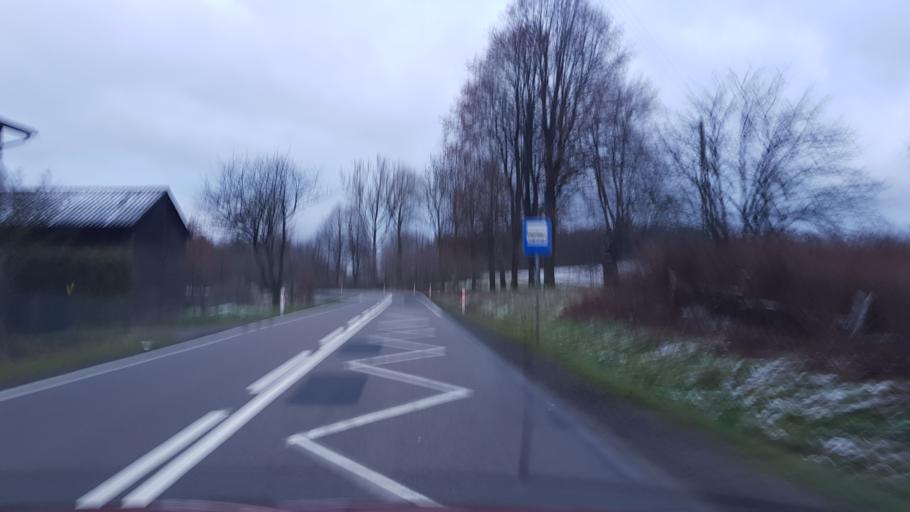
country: PL
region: Pomeranian Voivodeship
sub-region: Powiat bytowski
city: Tuchomie
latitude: 54.0853
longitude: 17.3024
